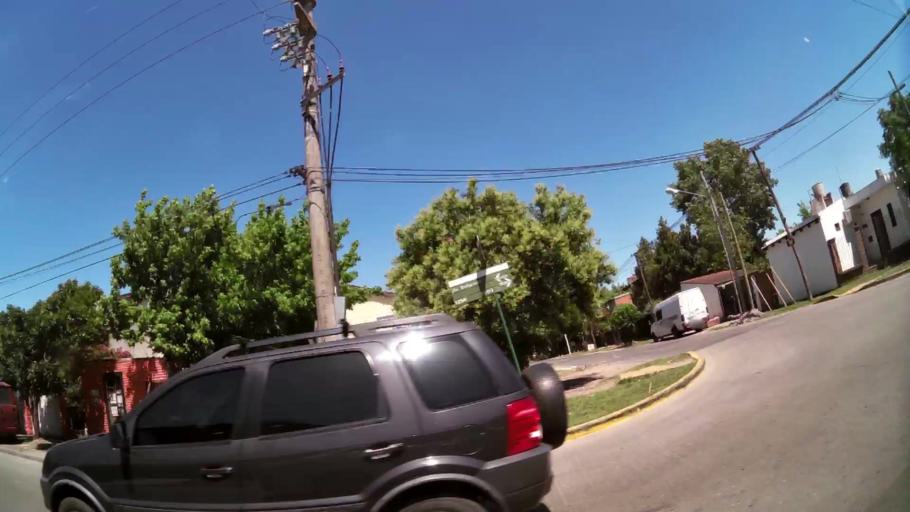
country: AR
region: Buenos Aires
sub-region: Partido de Tigre
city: Tigre
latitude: -34.4852
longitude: -58.6417
